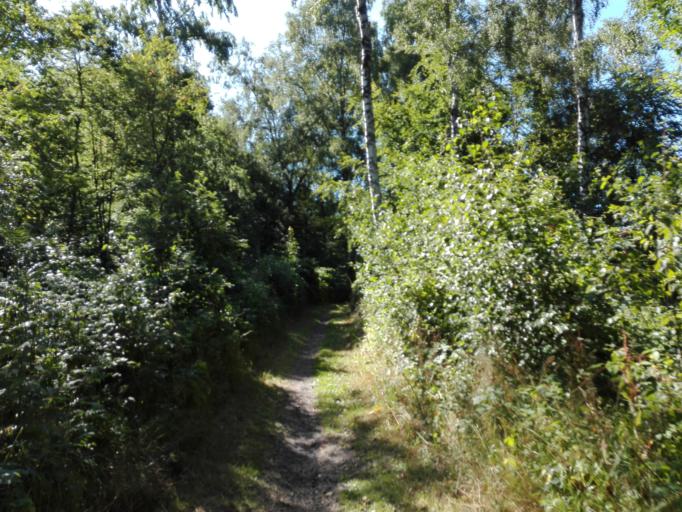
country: DK
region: Central Jutland
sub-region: Odder Kommune
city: Odder
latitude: 55.9681
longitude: 10.1415
